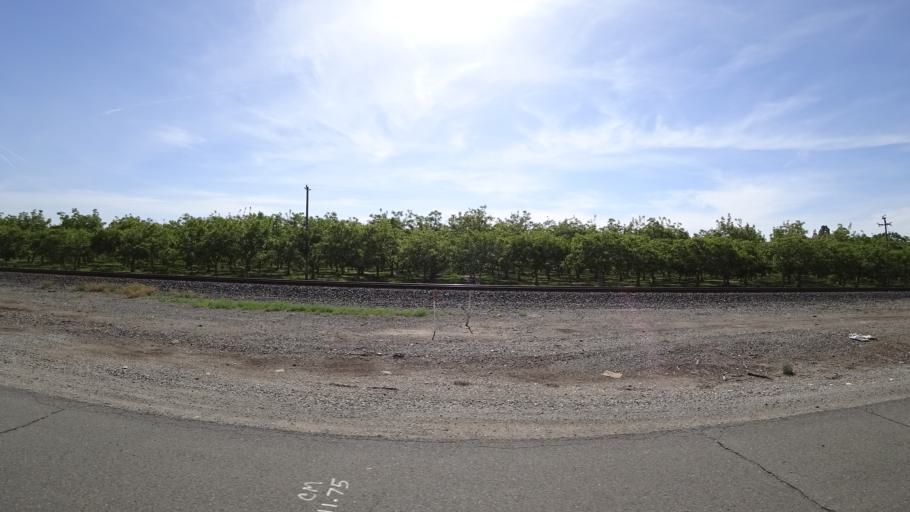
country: US
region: California
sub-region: Tehama County
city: Los Molinos
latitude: 40.0202
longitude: -122.0997
